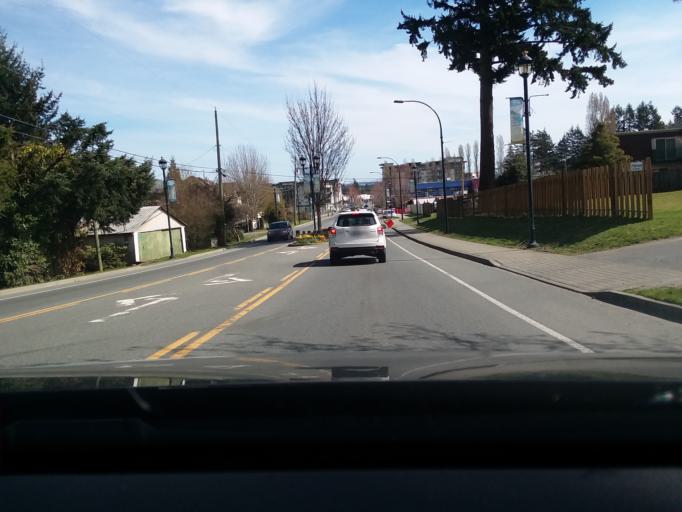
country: CA
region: British Columbia
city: Colwood
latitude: 48.4445
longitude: -123.4743
